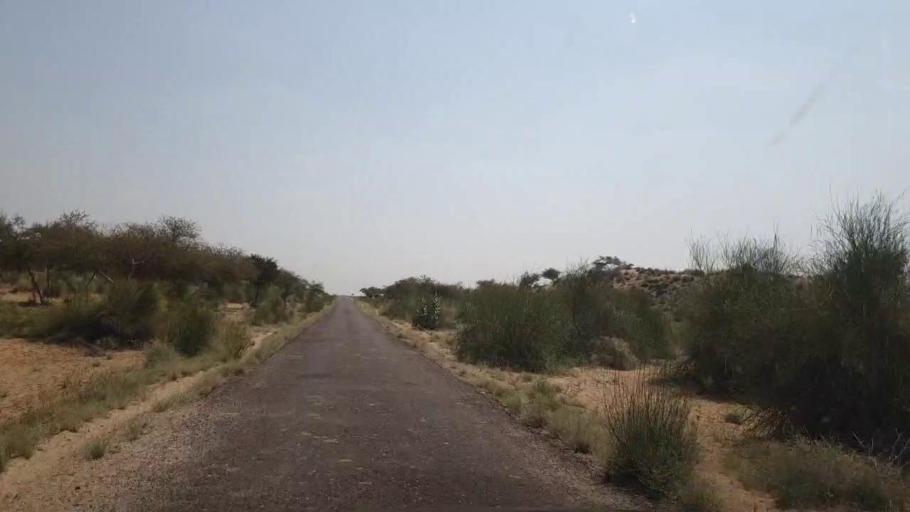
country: PK
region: Sindh
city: Islamkot
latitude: 25.0799
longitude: 70.7372
